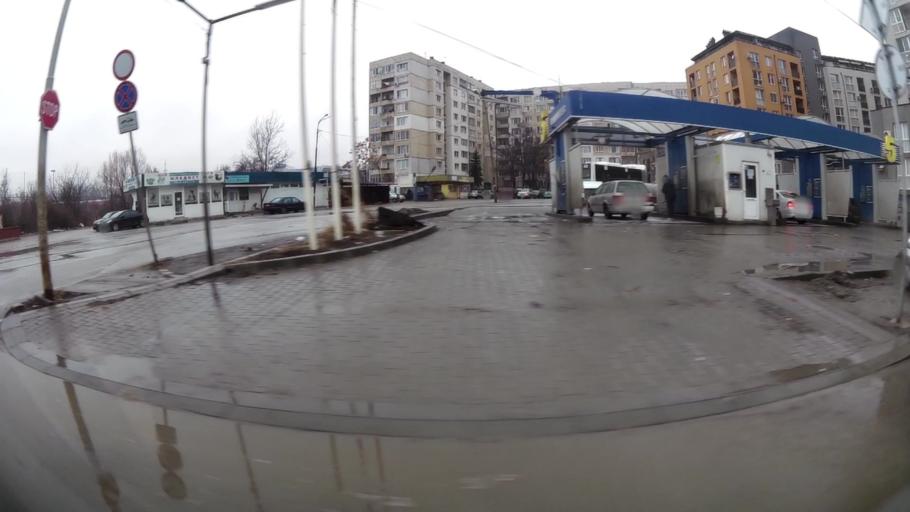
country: BG
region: Sofia-Capital
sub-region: Stolichna Obshtina
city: Sofia
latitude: 42.6257
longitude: 23.3848
